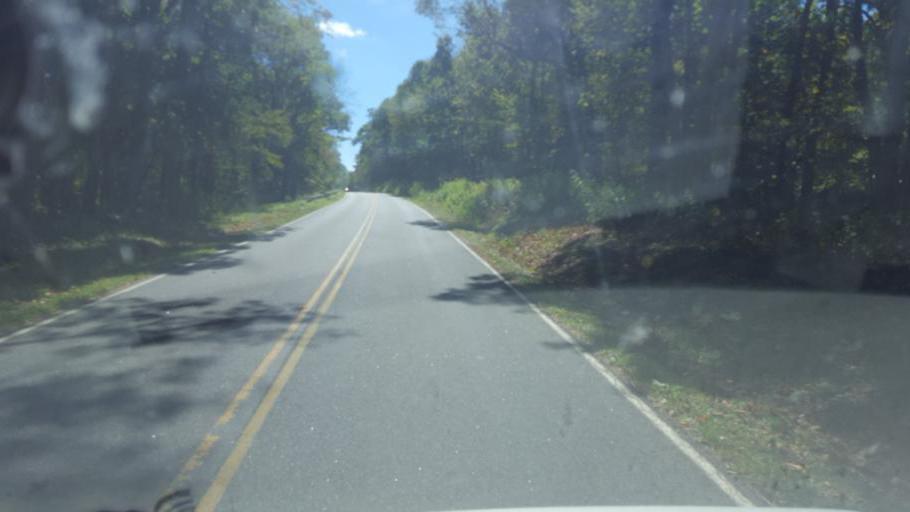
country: US
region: Virginia
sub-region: Page County
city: Stanley
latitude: 38.4681
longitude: -78.4576
